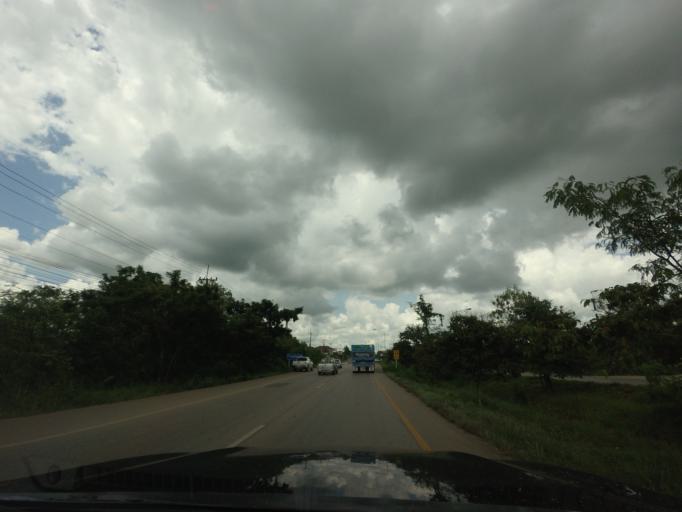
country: TH
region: Nong Khai
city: Sa Khrai
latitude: 17.5593
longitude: 102.8011
